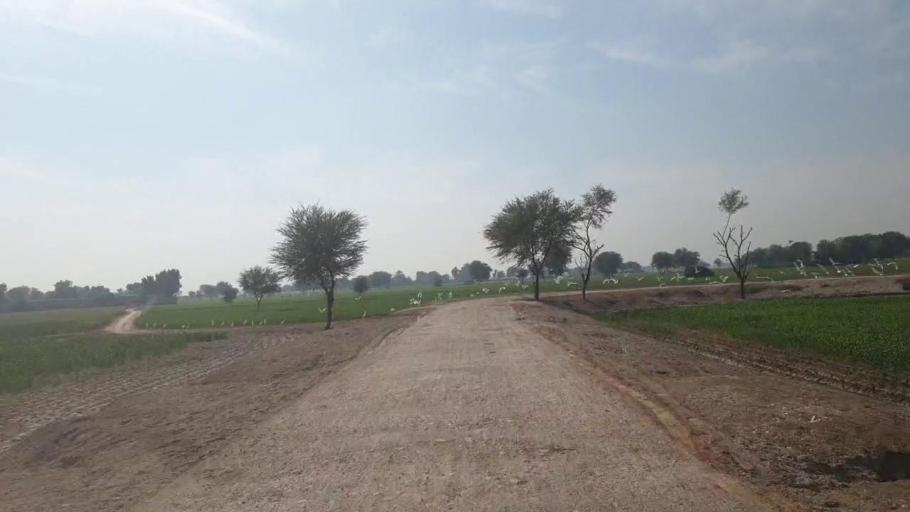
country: PK
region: Sindh
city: Nawabshah
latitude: 26.1620
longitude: 68.5090
